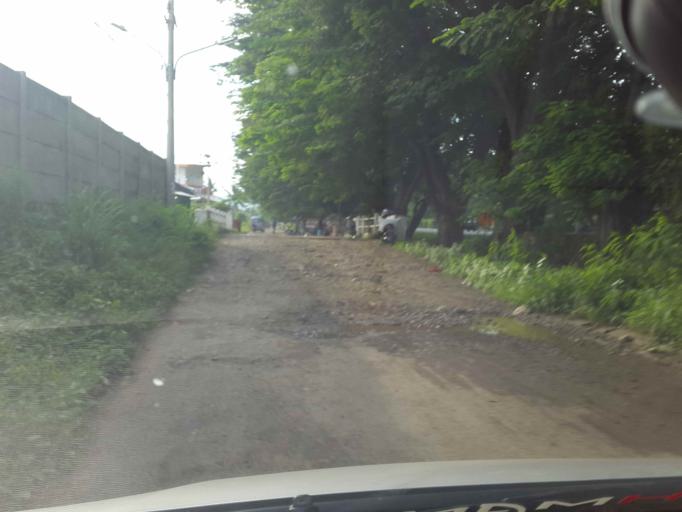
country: ID
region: Banten
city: Bojonegara
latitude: -6.0032
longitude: 106.0635
